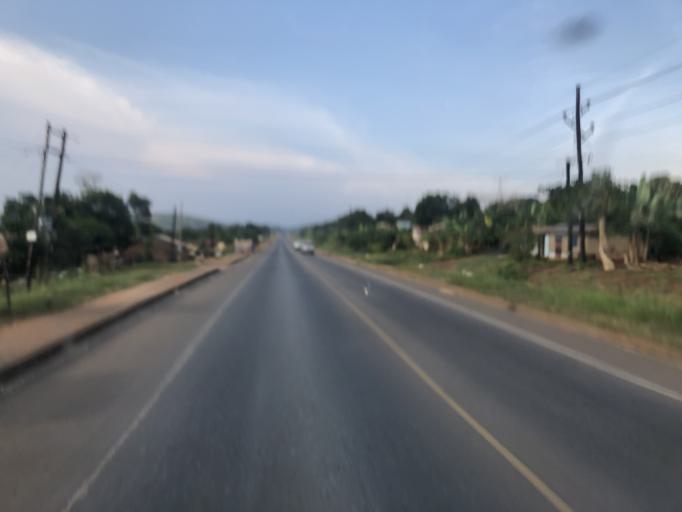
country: UG
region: Central Region
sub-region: Mpigi District
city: Mpigi
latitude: 0.1757
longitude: 32.2758
